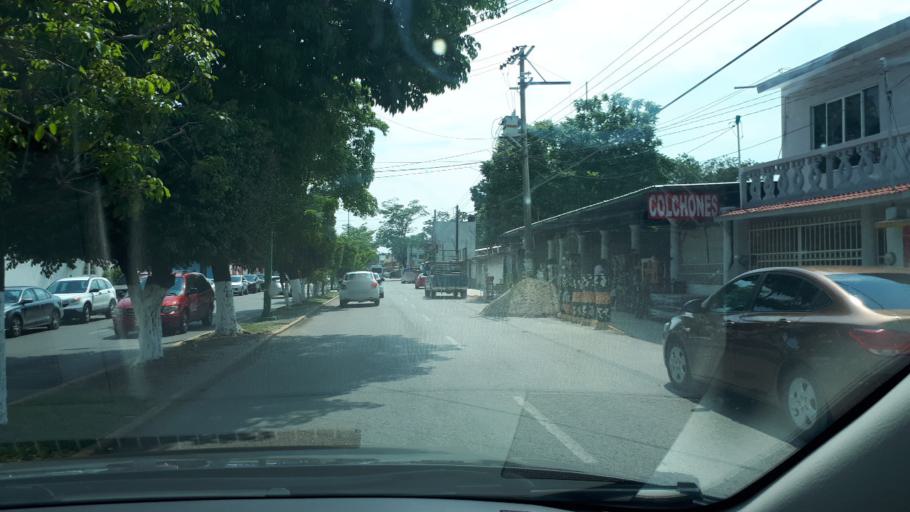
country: MX
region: Tabasco
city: Comalcalco
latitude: 18.2724
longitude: -93.2195
